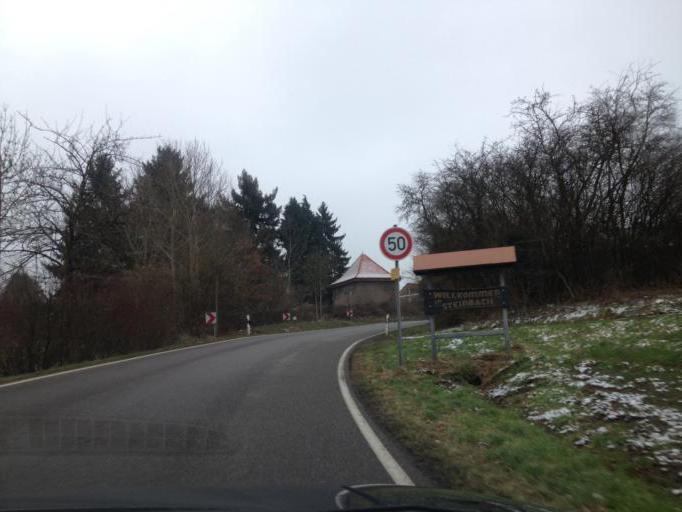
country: DE
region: Saarland
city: Hangard
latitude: 49.4112
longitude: 7.2090
